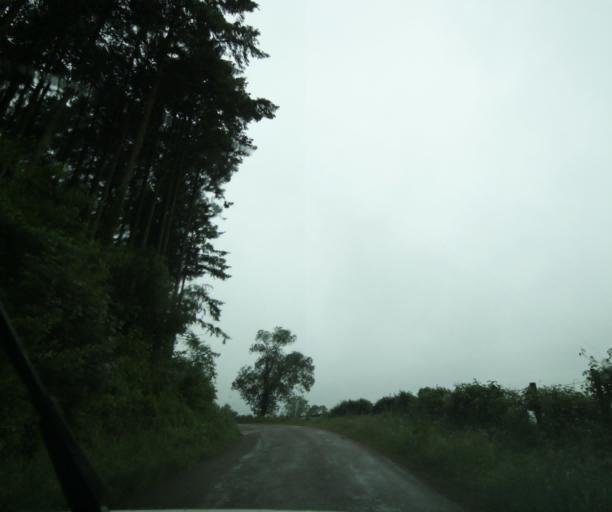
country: FR
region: Bourgogne
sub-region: Departement de Saone-et-Loire
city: Charolles
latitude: 46.3835
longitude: 4.3427
